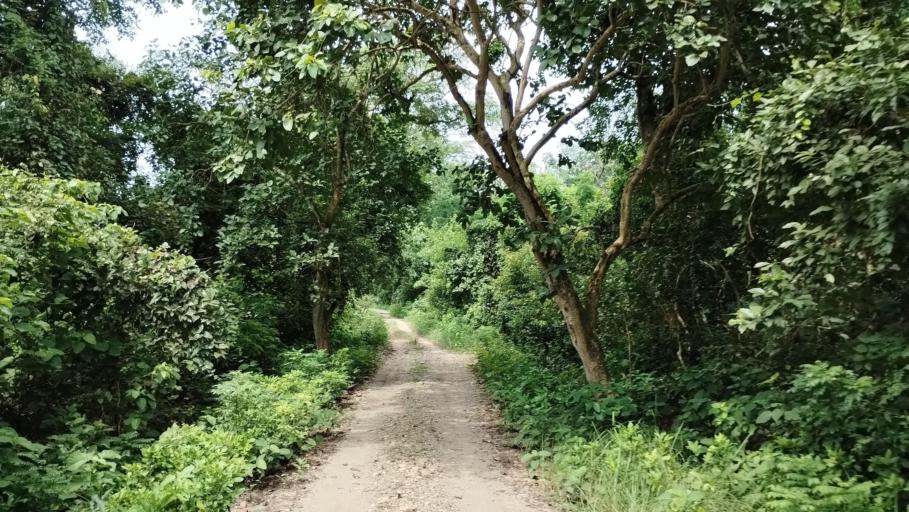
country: NP
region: Far Western
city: Tikapur
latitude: 28.4558
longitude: 81.2423
